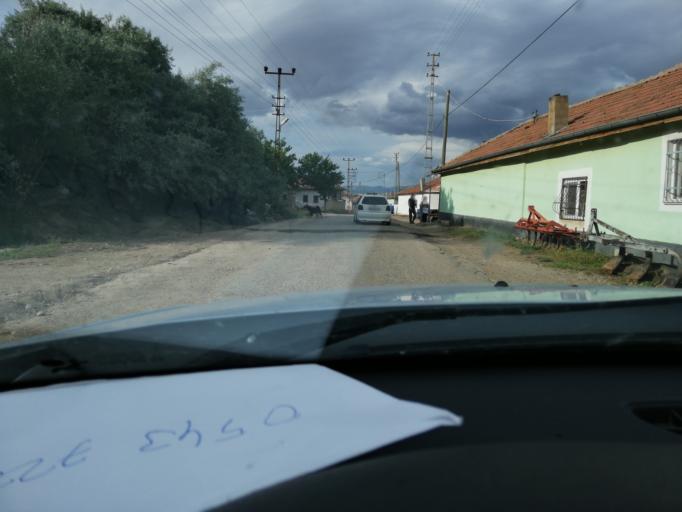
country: TR
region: Kirsehir
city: Kirsehir
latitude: 39.0260
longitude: 34.1255
